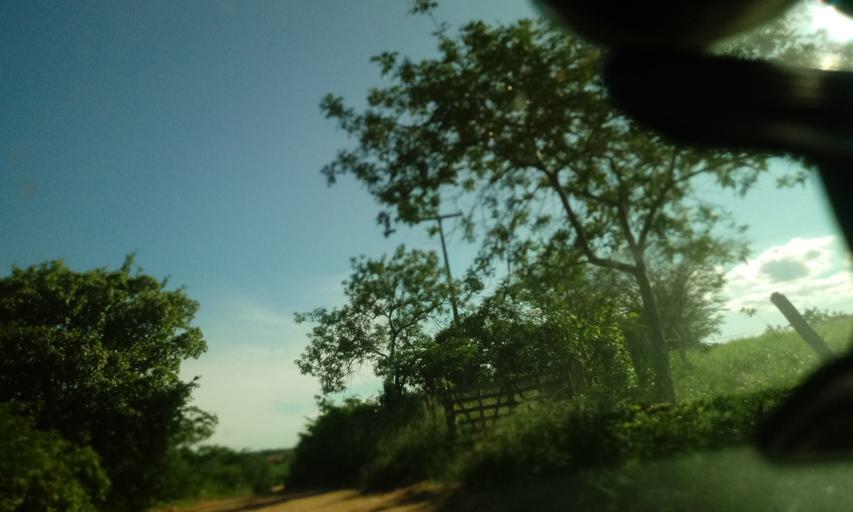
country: BR
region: Bahia
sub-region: Riacho De Santana
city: Riacho de Santana
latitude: -13.7949
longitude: -42.7327
